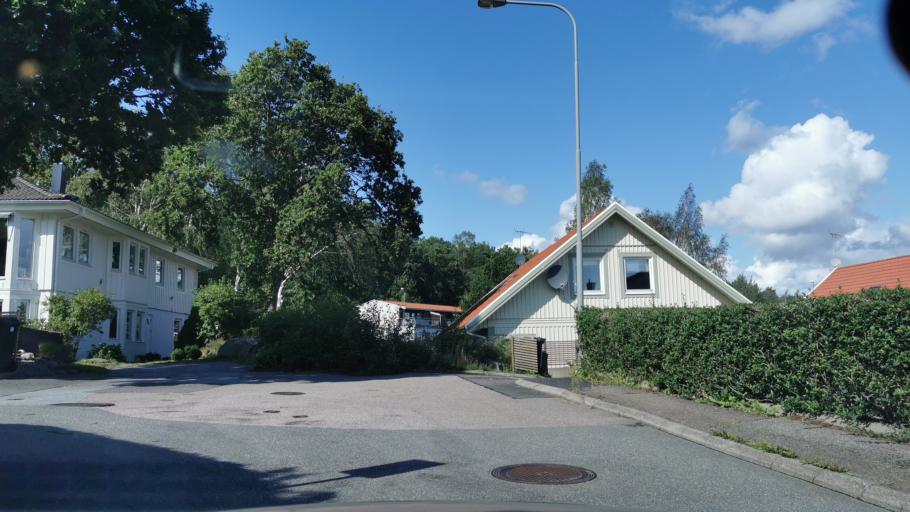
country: SE
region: Vaestra Goetaland
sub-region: Goteborg
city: Majorna
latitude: 57.6429
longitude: 11.9128
